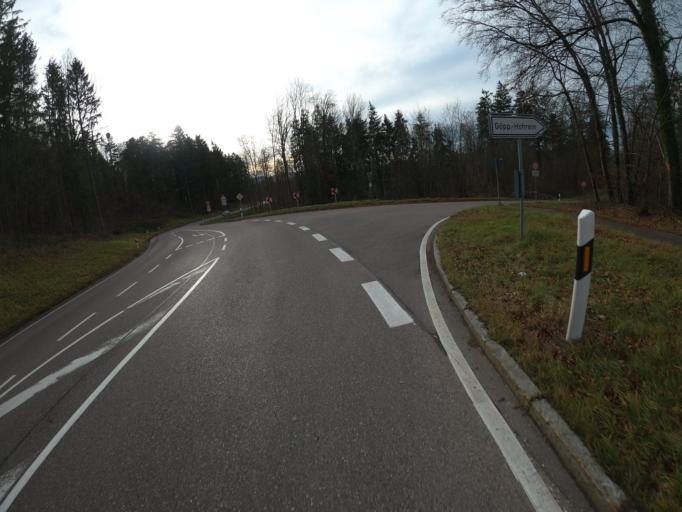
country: DE
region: Baden-Wuerttemberg
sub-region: Regierungsbezirk Stuttgart
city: Waschenbeuren
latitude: 48.7318
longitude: 9.7106
